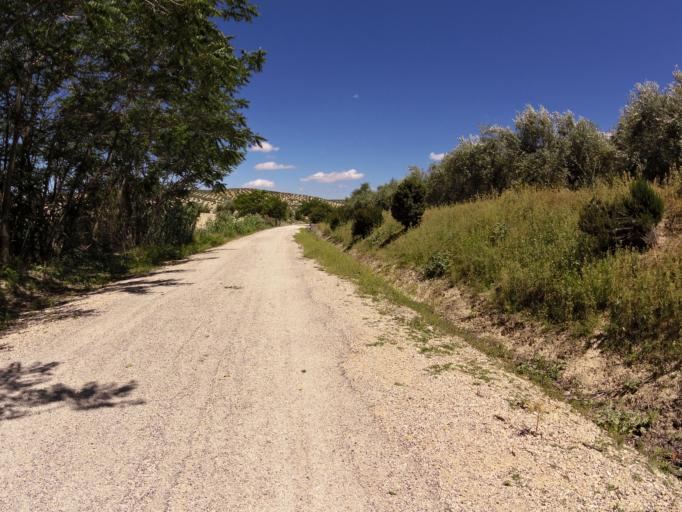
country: ES
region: Andalusia
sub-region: Provincia de Jaen
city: Jamilena
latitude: 37.7718
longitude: -3.9263
